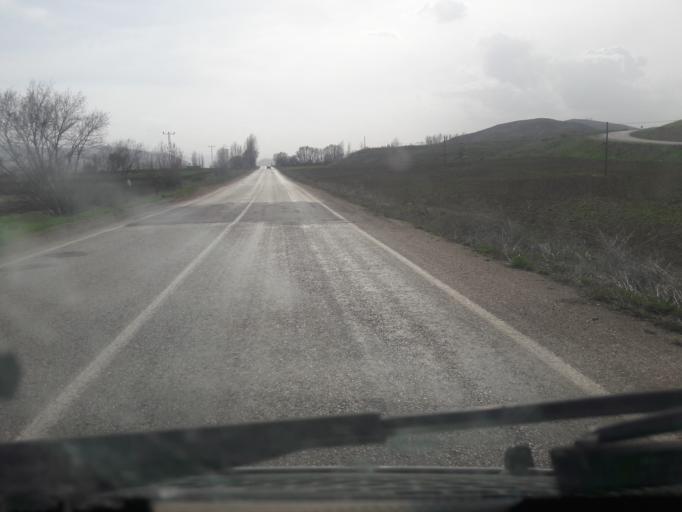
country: TR
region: Gumushane
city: Kelkit
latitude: 40.1422
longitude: 39.3992
